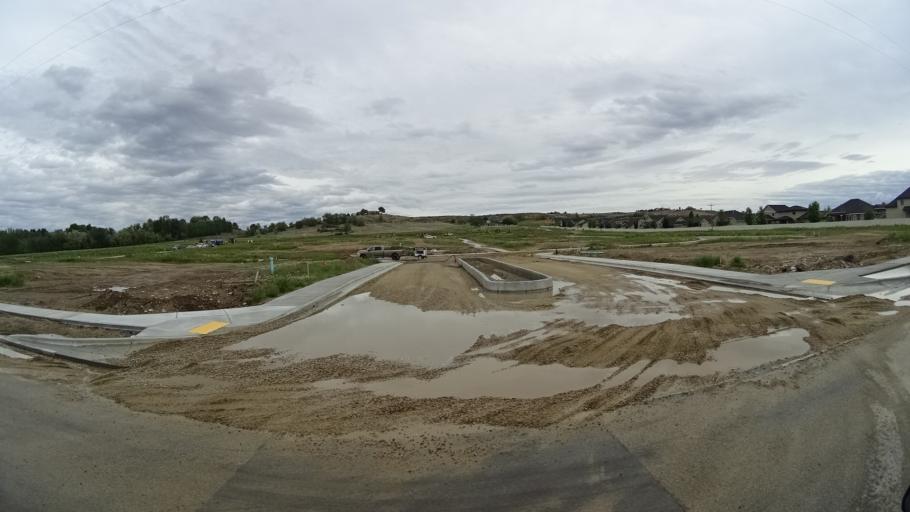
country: US
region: Idaho
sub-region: Ada County
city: Star
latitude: 43.7173
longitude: -116.4995
